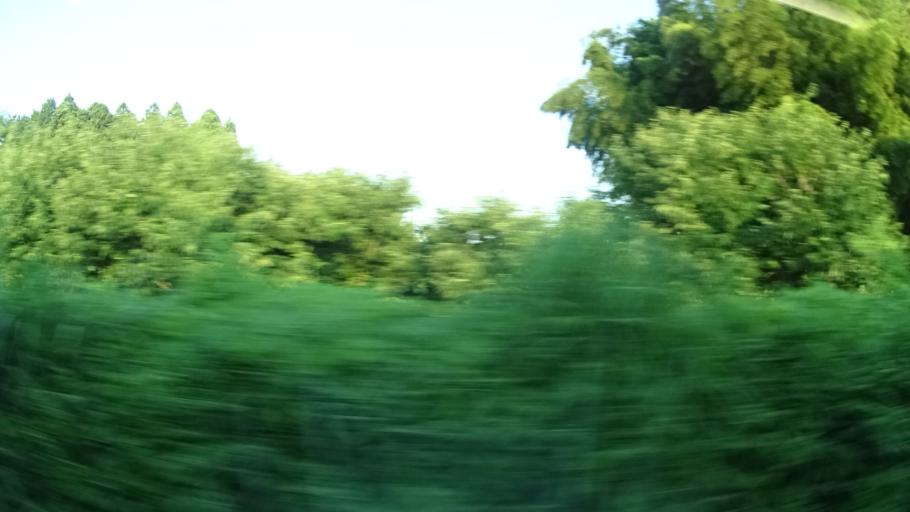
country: JP
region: Ibaraki
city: Tomobe
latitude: 36.3078
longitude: 140.2864
